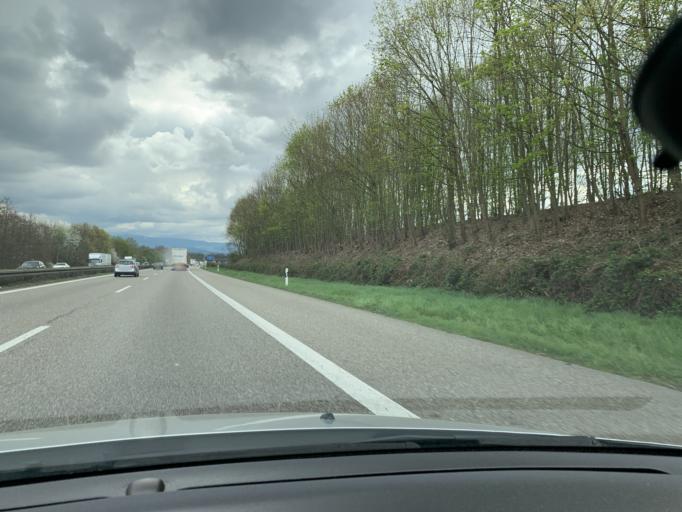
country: DE
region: Baden-Wuerttemberg
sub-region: Freiburg Region
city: Vorstetten
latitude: 48.0698
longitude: 7.8103
